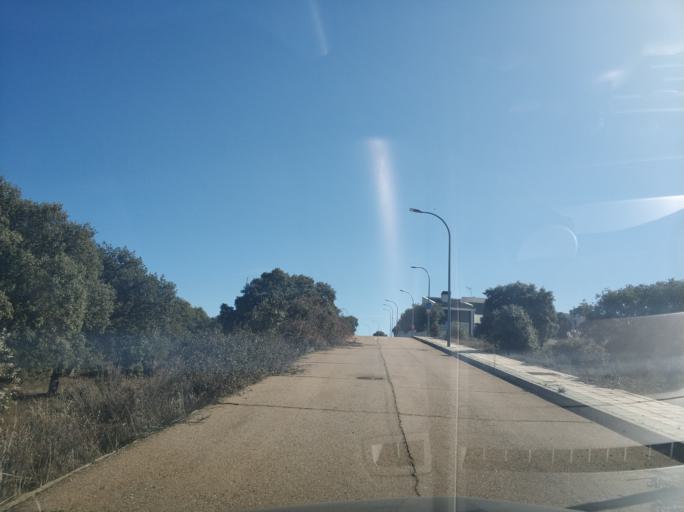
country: ES
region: Castille and Leon
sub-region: Provincia de Salamanca
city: Doninos de Salamanca
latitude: 40.9347
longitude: -5.7444
